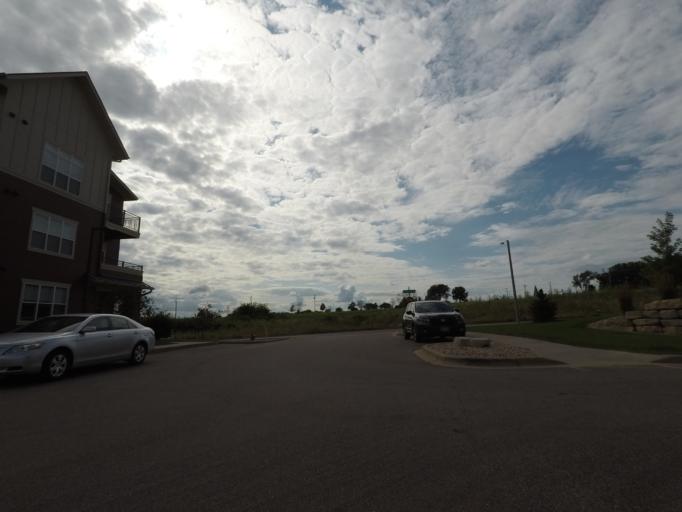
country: US
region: Wisconsin
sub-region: Dane County
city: Middleton
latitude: 43.0583
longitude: -89.5496
